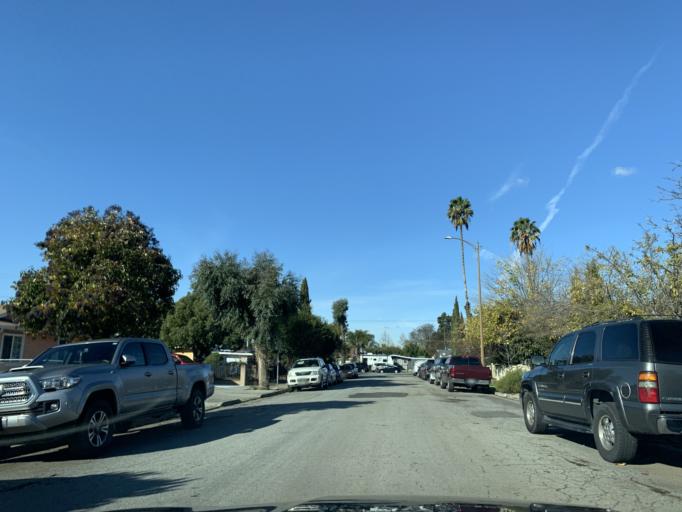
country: US
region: California
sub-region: Santa Clara County
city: Alum Rock
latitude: 37.3368
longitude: -121.8377
